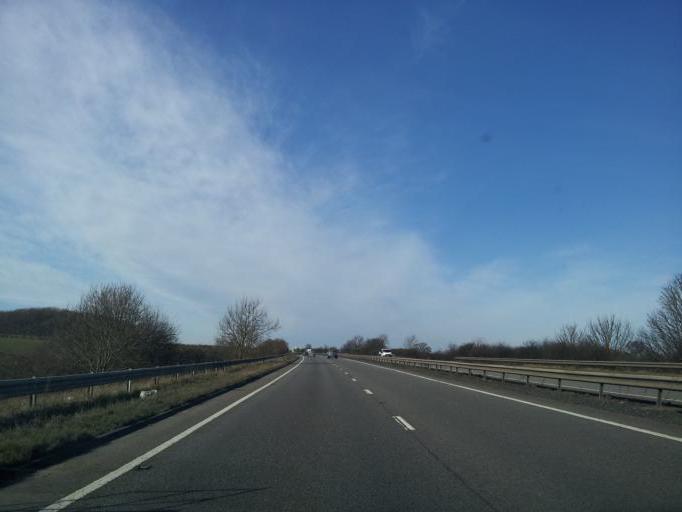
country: GB
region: England
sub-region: Lincolnshire
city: Grantham
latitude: 52.8815
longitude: -0.6366
